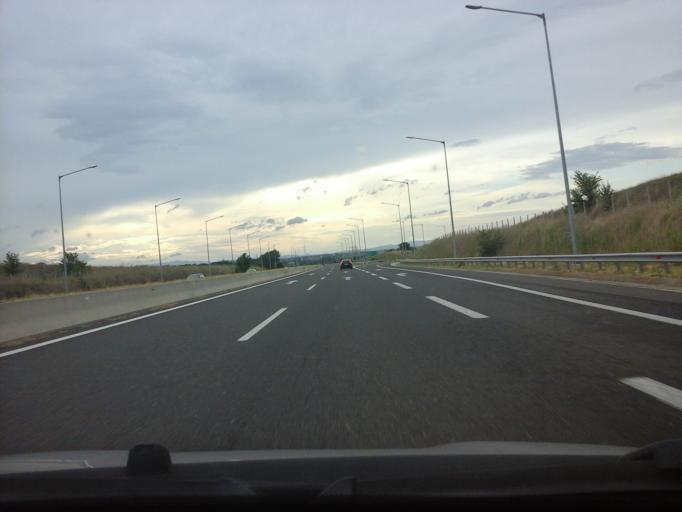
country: GR
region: East Macedonia and Thrace
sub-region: Nomos Rodopis
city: Komotini
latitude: 41.1032
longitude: 25.3548
